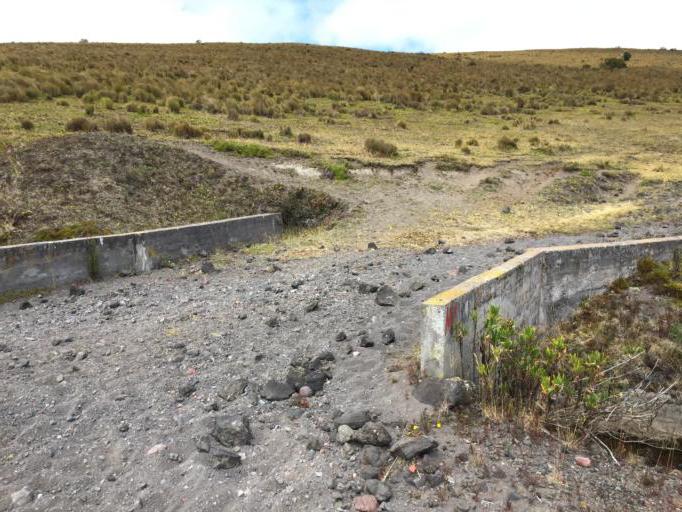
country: EC
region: Pichincha
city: Machachi
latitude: -0.6120
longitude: -78.4370
